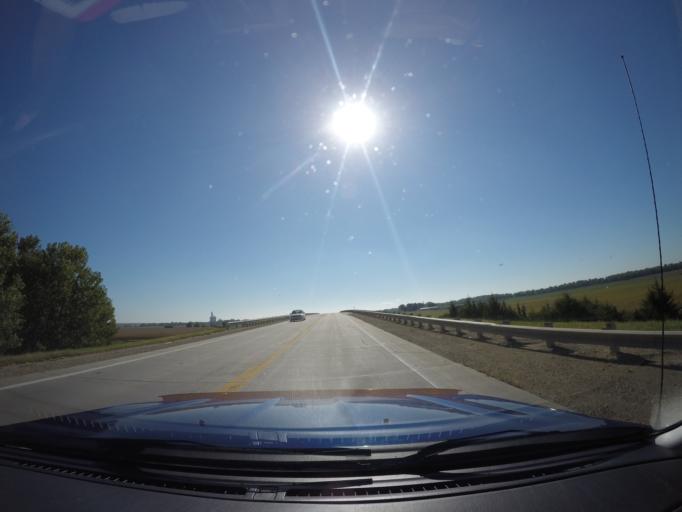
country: US
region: Kansas
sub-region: Pottawatomie County
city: Wamego
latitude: 39.2170
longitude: -96.2005
